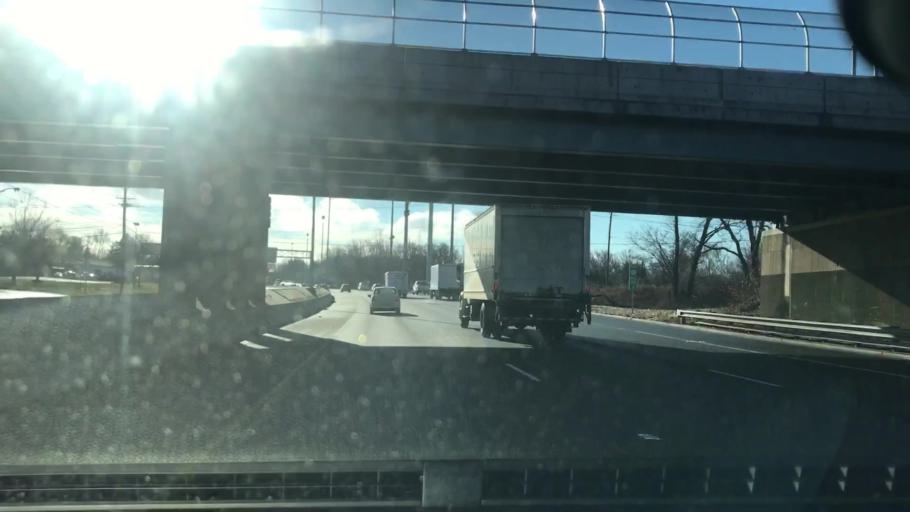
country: US
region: New Jersey
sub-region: Bergen County
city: Mahwah
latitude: 41.0811
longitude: -74.1504
